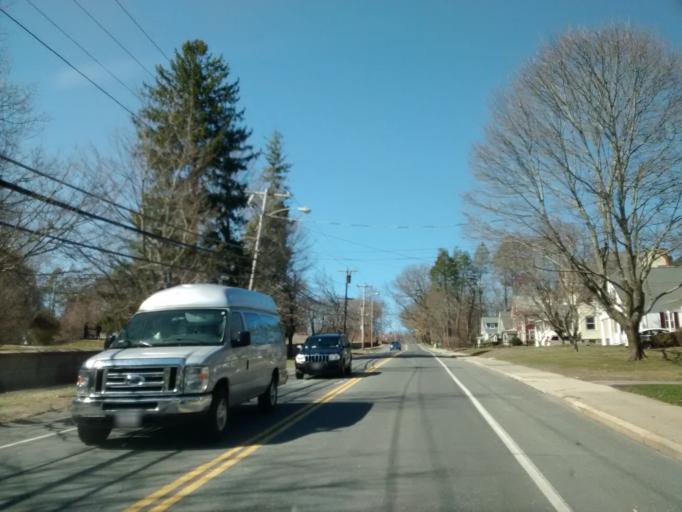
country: US
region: Massachusetts
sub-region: Worcester County
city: Whitinsville
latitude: 42.1116
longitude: -71.6658
